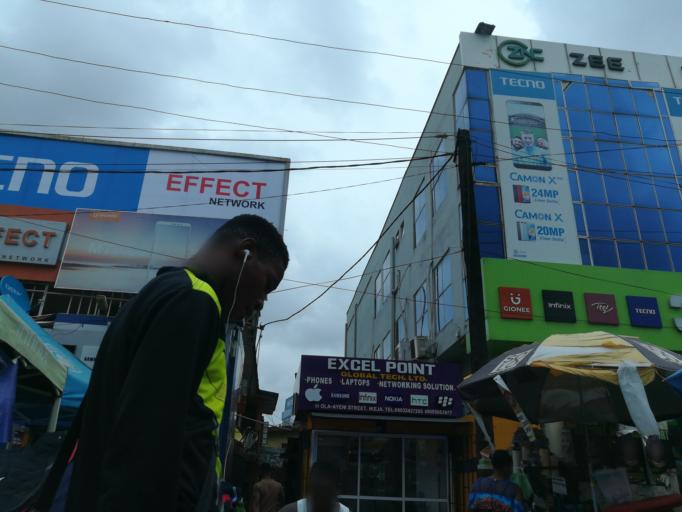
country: NG
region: Lagos
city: Ikeja
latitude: 6.5949
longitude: 3.3395
